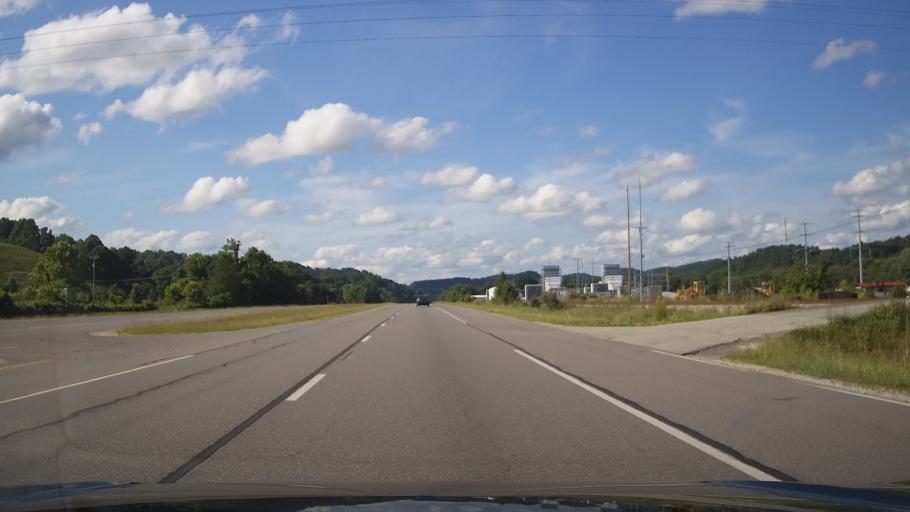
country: US
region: Kentucky
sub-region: Lawrence County
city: Louisa
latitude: 38.1858
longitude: -82.6073
